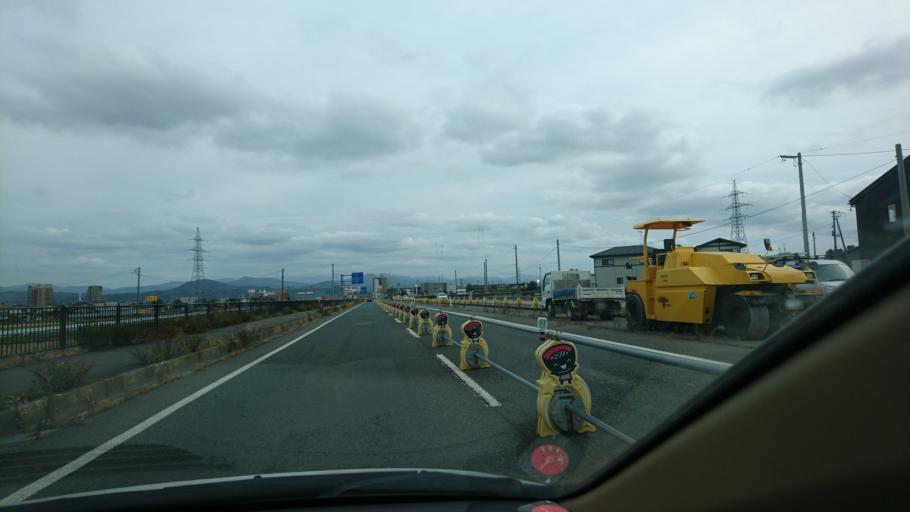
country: JP
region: Iwate
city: Morioka-shi
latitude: 39.6880
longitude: 141.1156
